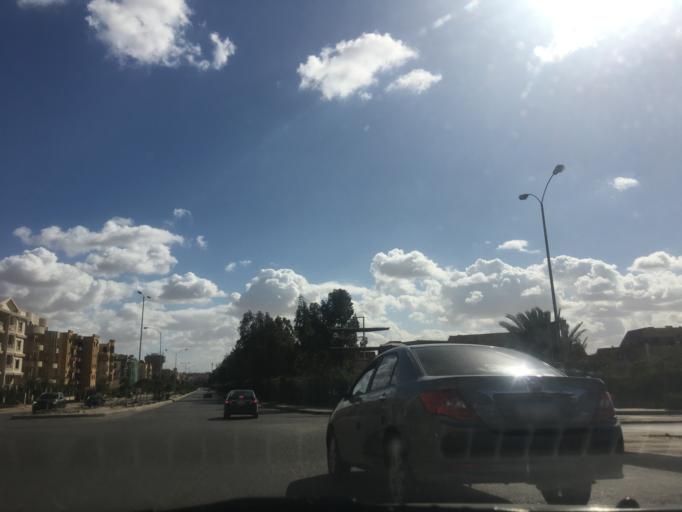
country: EG
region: Al Jizah
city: Madinat Sittah Uktubar
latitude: 29.9995
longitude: 30.9750
